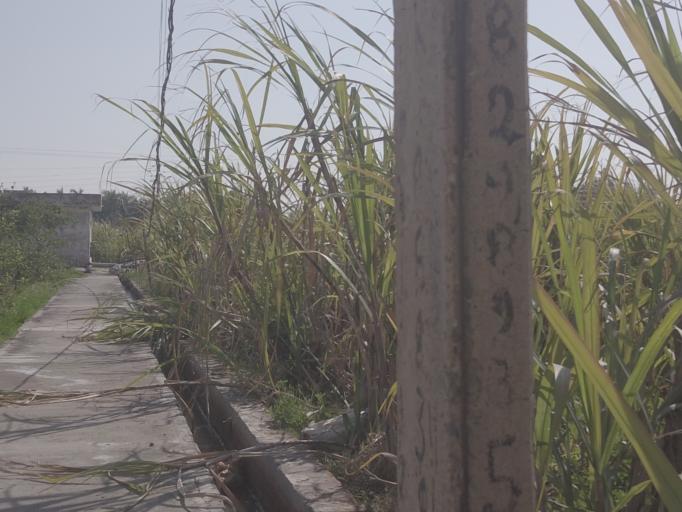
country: IN
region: Punjab
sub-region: Shahid Bhagat Singh Nagar
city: Rahon
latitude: 31.0231
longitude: 76.0919
